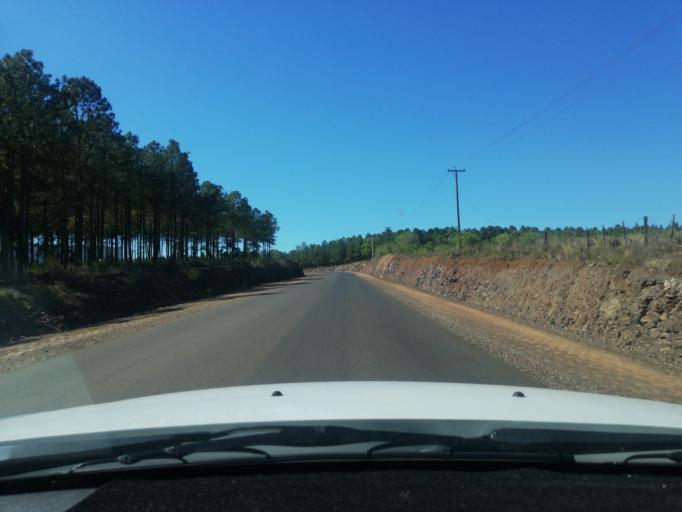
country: AR
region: Misiones
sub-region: Departamento de Candelaria
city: Candelaria
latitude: -27.5089
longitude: -55.7364
